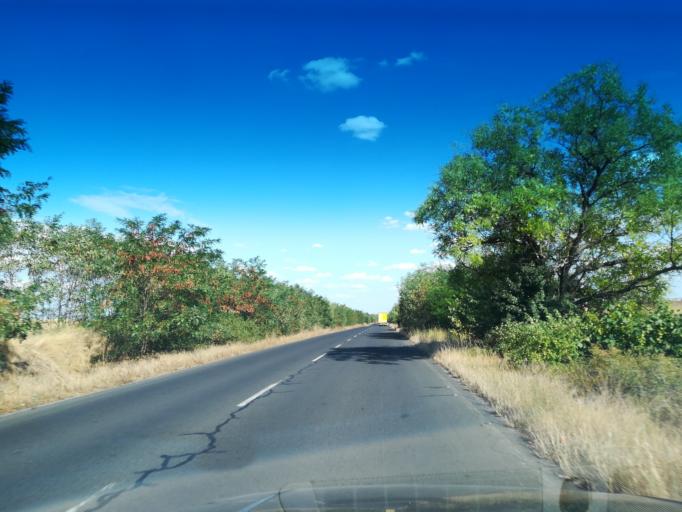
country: BG
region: Khaskovo
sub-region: Obshtina Mineralni Bani
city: Mineralni Bani
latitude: 42.0559
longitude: 25.3009
